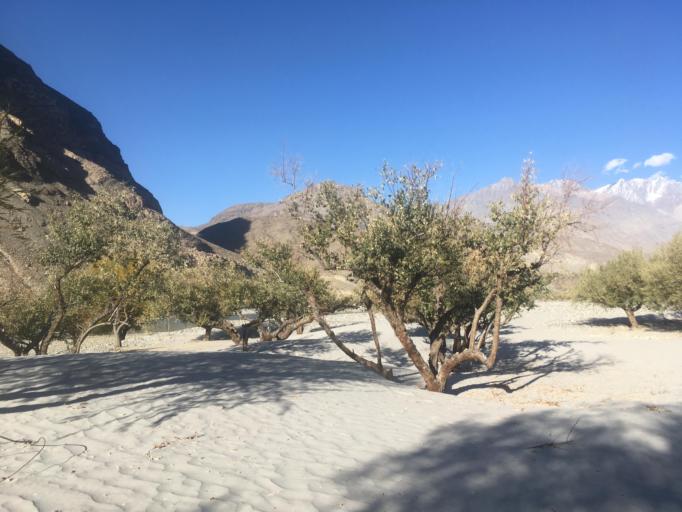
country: PK
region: Gilgit-Baltistan
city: Skardu
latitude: 35.3180
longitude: 75.6885
